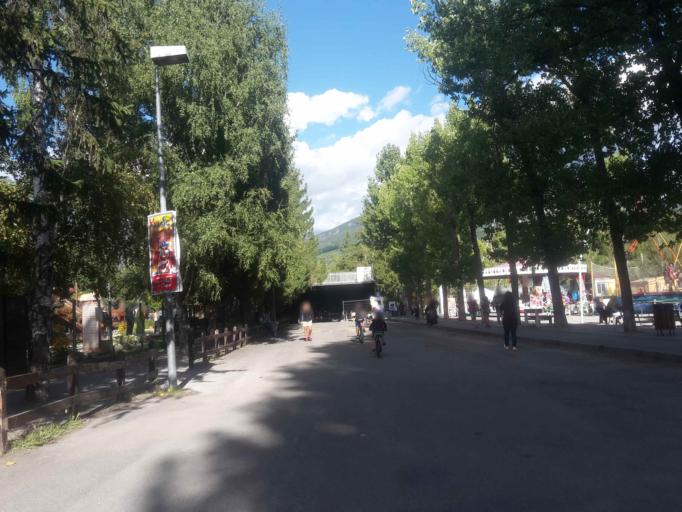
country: FR
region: Provence-Alpes-Cote d'Azur
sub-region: Departement des Hautes-Alpes
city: Embrun
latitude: 44.5508
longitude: 6.4782
